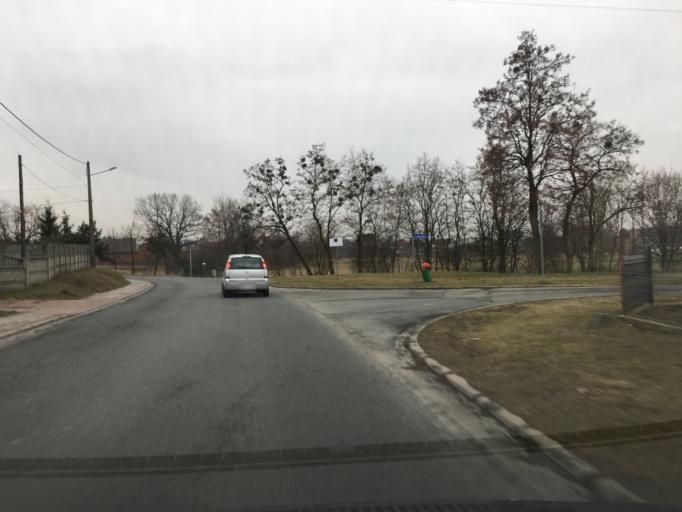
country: PL
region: Opole Voivodeship
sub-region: Powiat kedzierzynsko-kozielski
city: Bierawa
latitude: 50.2845
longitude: 18.2390
